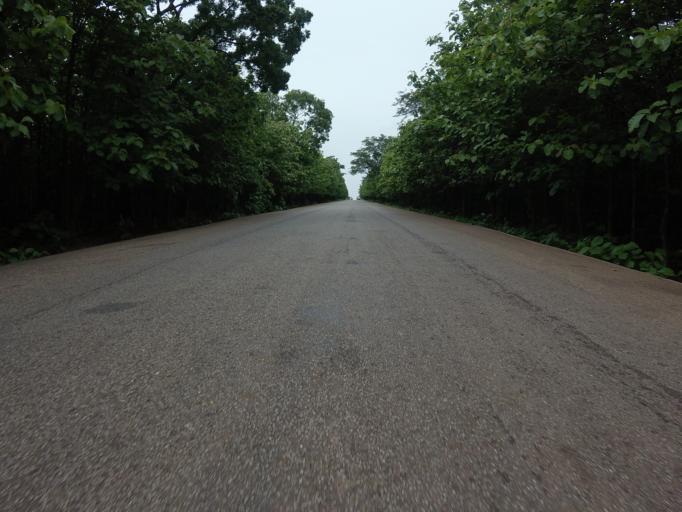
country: GH
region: Northern
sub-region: Yendi
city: Yendi
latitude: 9.4326
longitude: -0.0080
